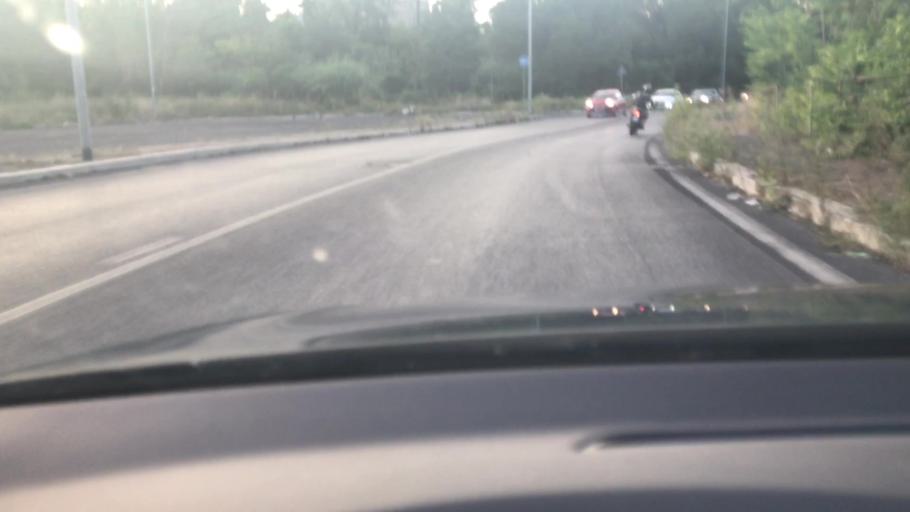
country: IT
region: Latium
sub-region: Citta metropolitana di Roma Capitale
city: Rome
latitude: 41.9259
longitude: 12.5636
